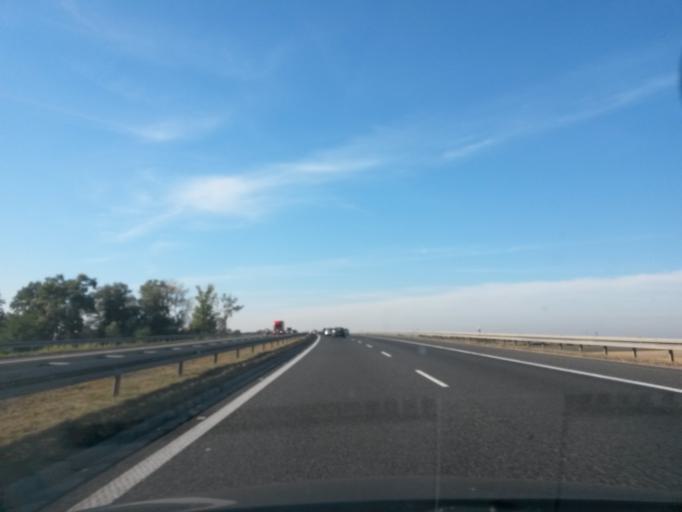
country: PL
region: Lower Silesian Voivodeship
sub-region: Powiat wroclawski
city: Zorawina
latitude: 50.9896
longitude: 17.0545
